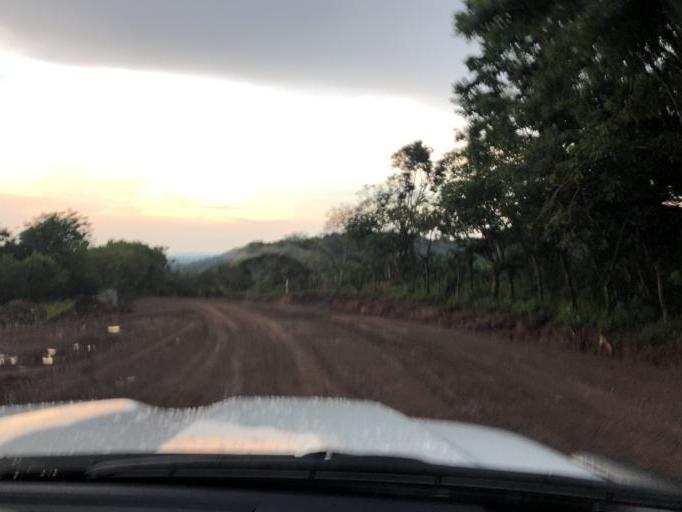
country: NI
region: Chontales
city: La Libertad
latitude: 12.1829
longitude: -85.1734
